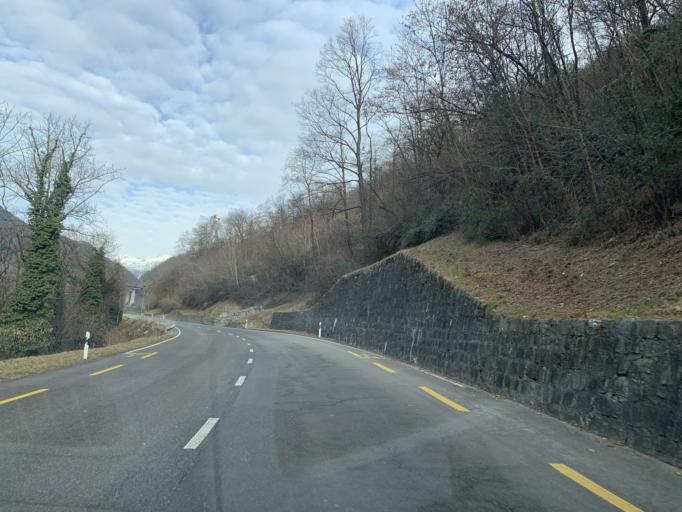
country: CH
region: Ticino
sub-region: Leventina District
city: Bodio
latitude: 46.4112
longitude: 8.8688
